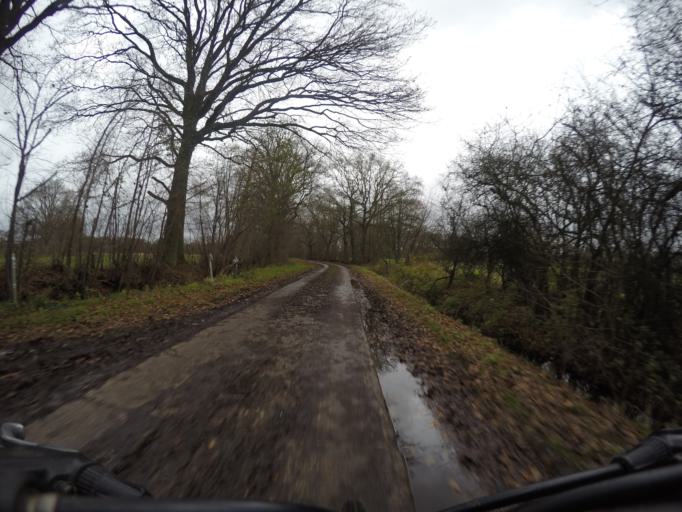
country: DE
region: Schleswig-Holstein
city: Hemdingen
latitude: 53.7261
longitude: 9.8350
